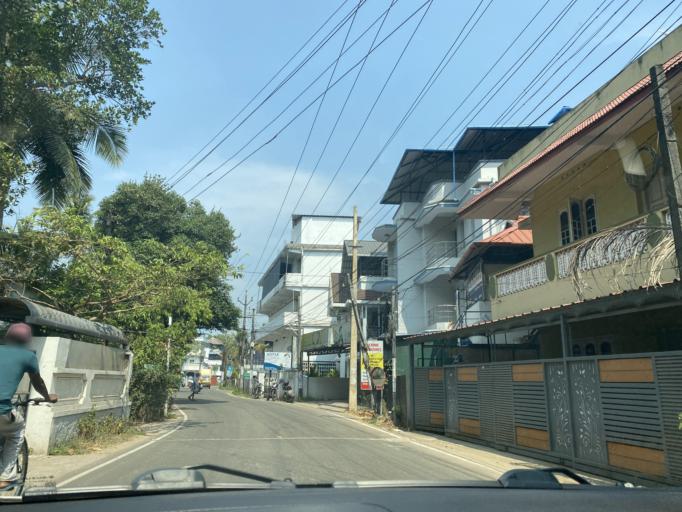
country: IN
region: Kerala
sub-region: Alappuzha
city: Arukutti
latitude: 9.9063
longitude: 76.3199
